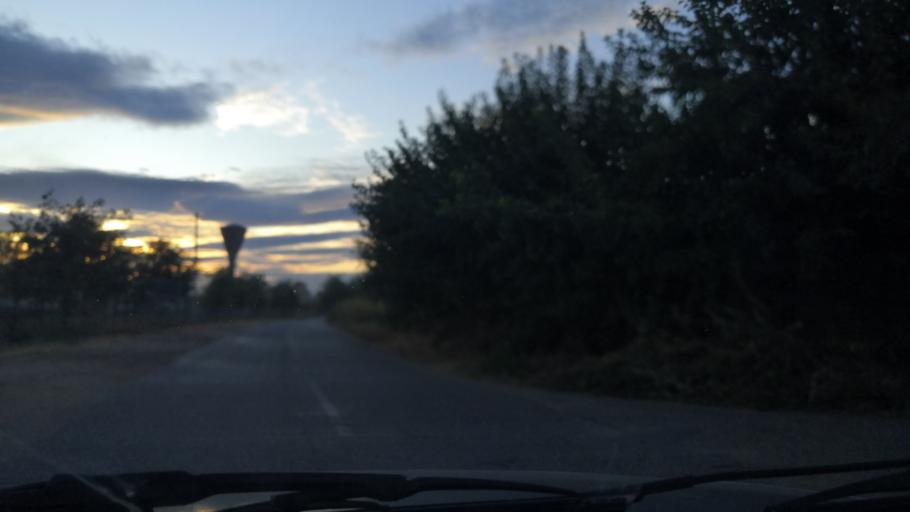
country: RO
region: Mehedinti
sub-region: Comuna Gruia
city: Izvoarele
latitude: 44.2889
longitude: 22.6124
